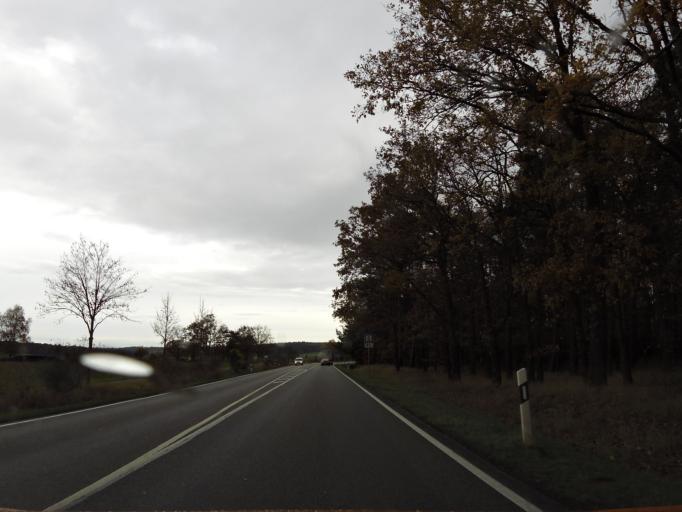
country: DE
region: Saxony-Anhalt
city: Kalbe
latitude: 52.6019
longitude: 11.3269
